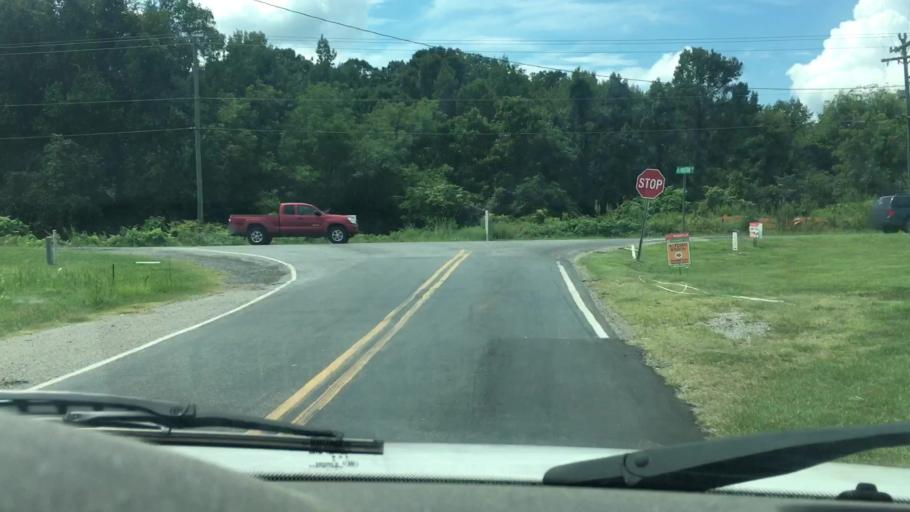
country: US
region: North Carolina
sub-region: Iredell County
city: Troutman
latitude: 35.6796
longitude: -80.8589
